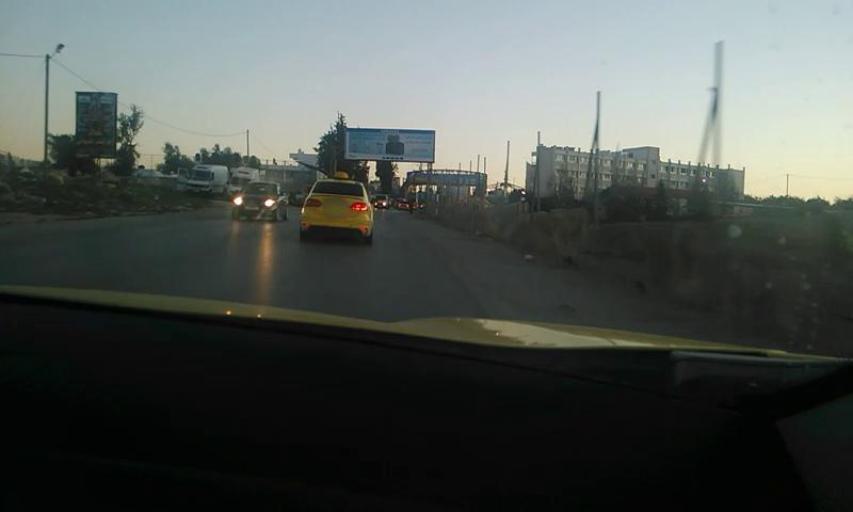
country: PS
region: West Bank
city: Surda
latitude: 31.9464
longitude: 35.2158
